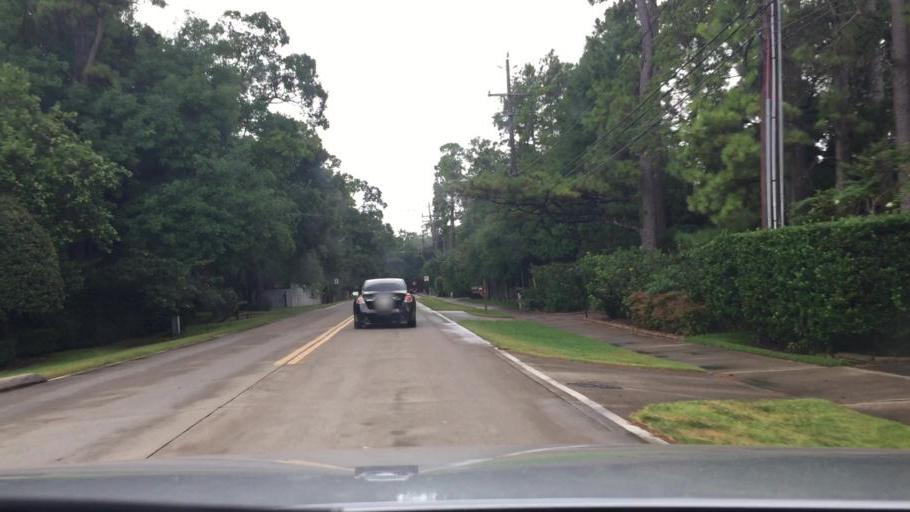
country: US
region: Texas
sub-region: Harris County
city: Hedwig Village
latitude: 29.7755
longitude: -95.5213
